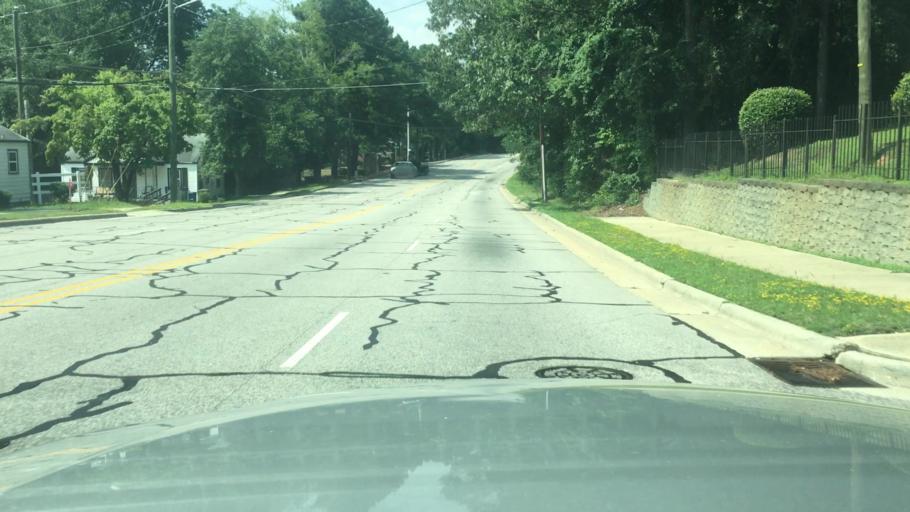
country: US
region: North Carolina
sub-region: Cumberland County
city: Fayetteville
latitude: 35.0836
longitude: -78.8827
